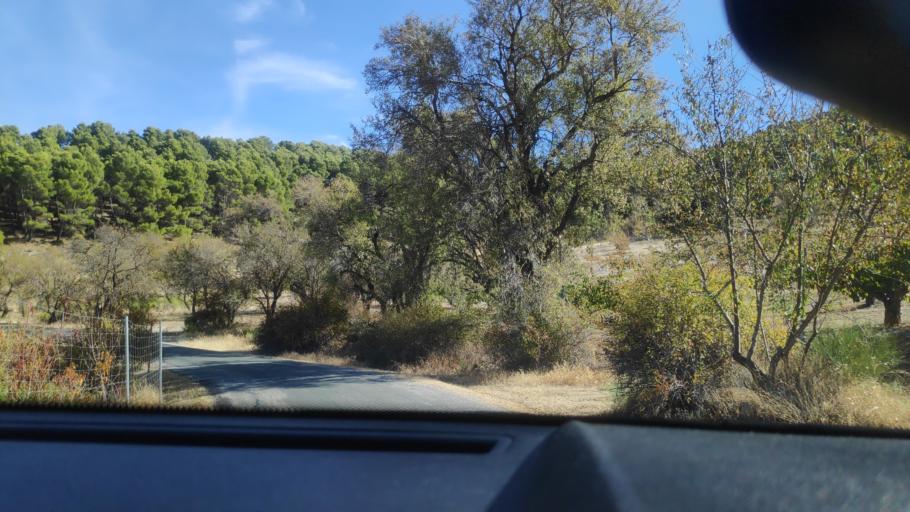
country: ES
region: Andalusia
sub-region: Provincia de Jaen
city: Torres
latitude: 37.7821
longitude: -3.4946
